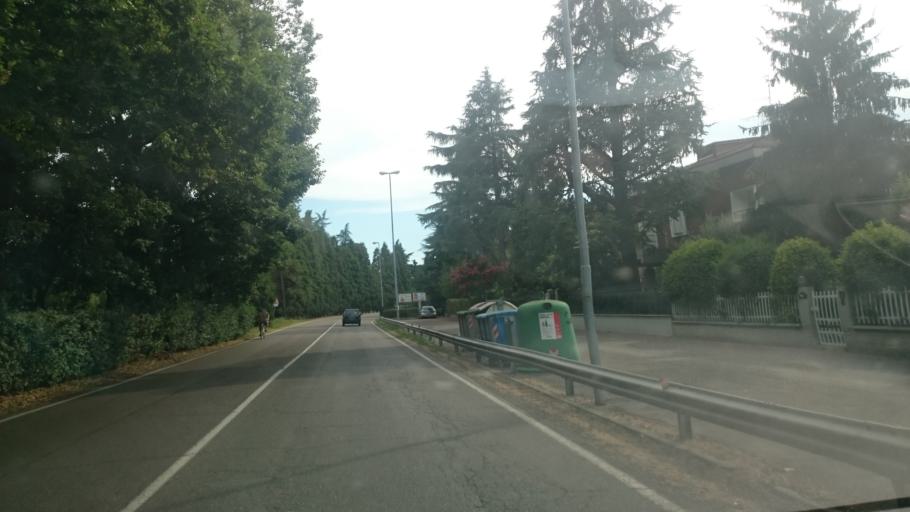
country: IT
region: Emilia-Romagna
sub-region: Provincia di Reggio Emilia
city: Reggio nell'Emilia
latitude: 44.6765
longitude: 10.6161
